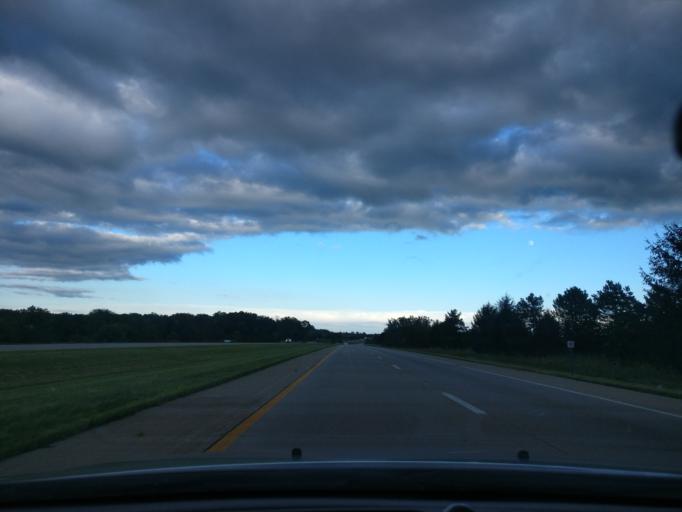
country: US
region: Ohio
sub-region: Greene County
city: Shawnee Hills
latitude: 39.6785
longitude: -83.8201
